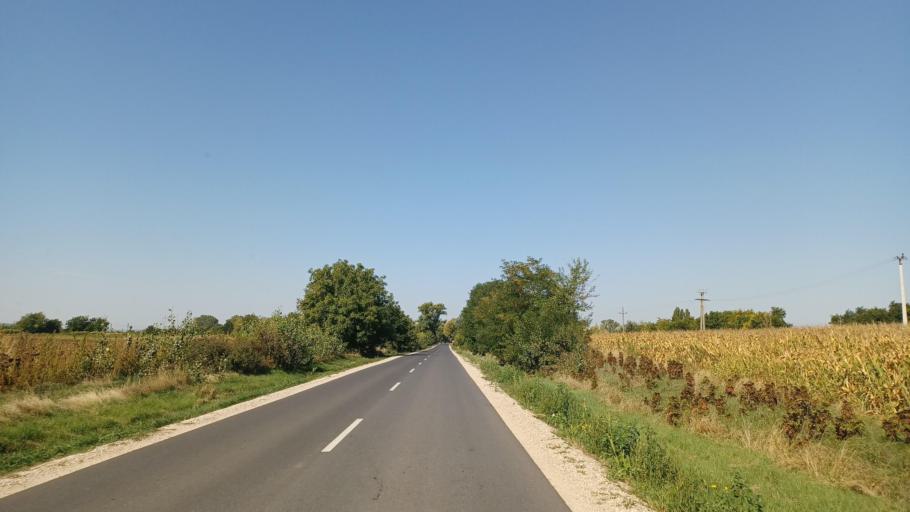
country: HU
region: Fejer
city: Cece
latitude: 46.7621
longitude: 18.6481
